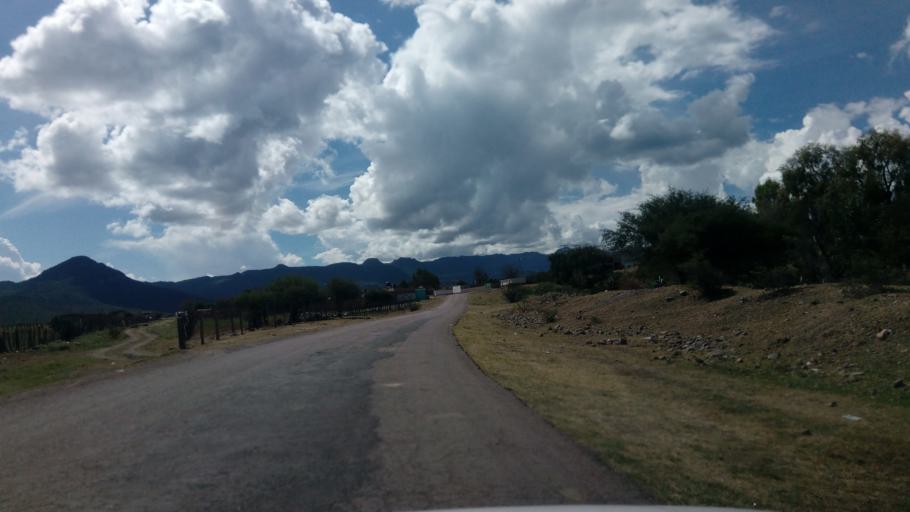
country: MX
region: Durango
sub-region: Durango
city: Jose Refugio Salcido
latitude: 23.7957
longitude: -104.4859
